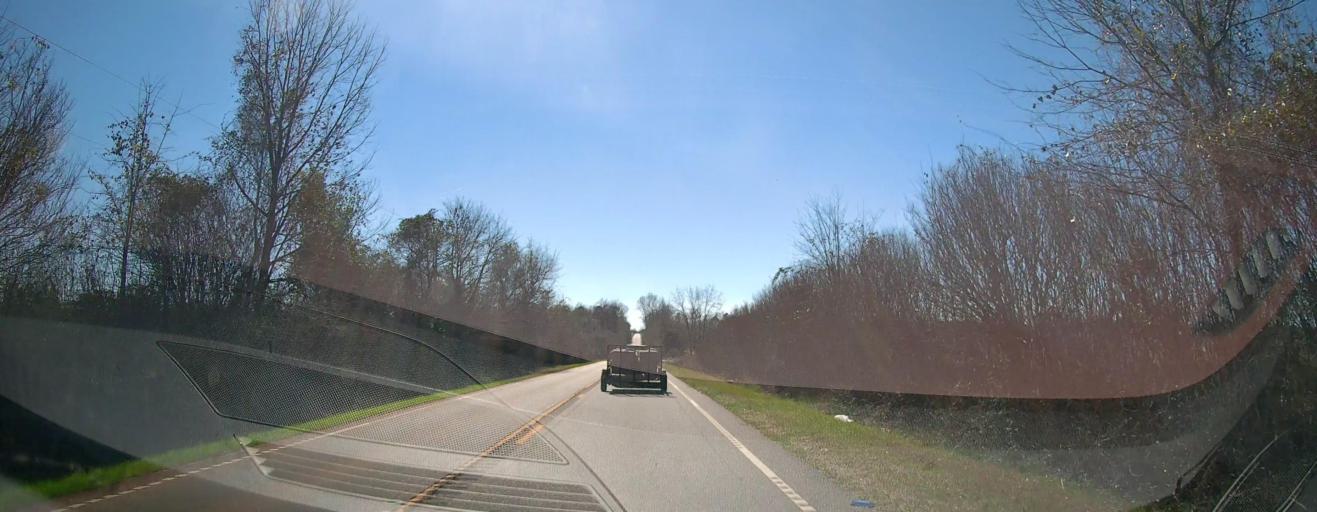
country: US
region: Georgia
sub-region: Macon County
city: Marshallville
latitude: 32.4446
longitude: -83.9863
